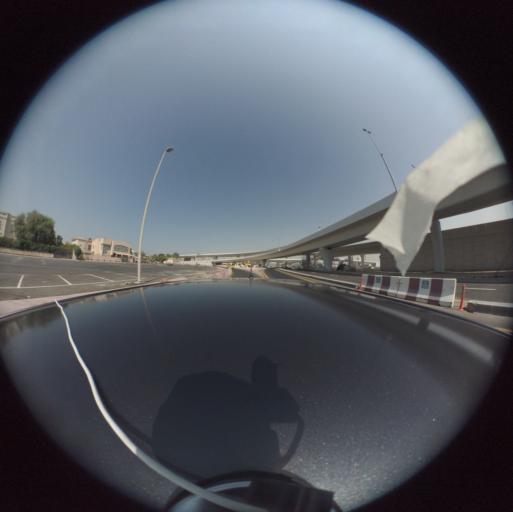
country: AE
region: Dubai
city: Dubai
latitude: 25.1639
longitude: 55.2334
